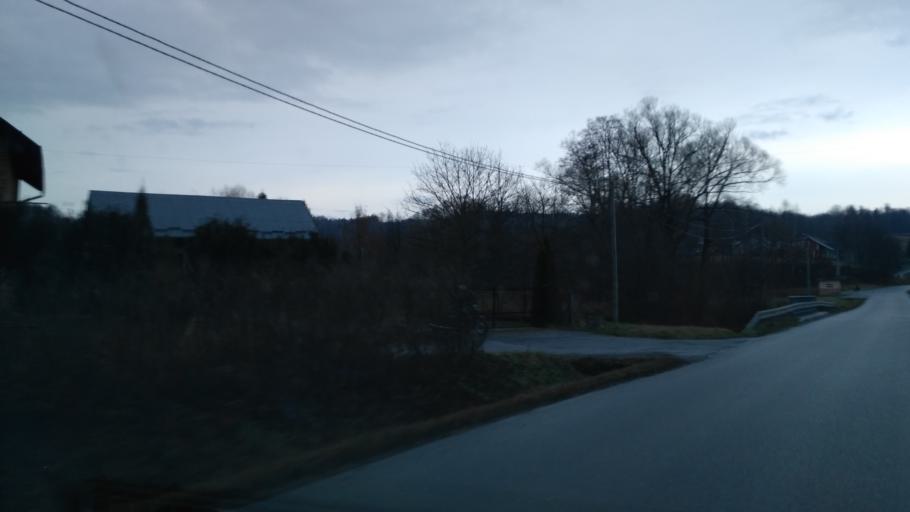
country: PL
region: Subcarpathian Voivodeship
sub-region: Powiat strzyzowski
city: Gwoznica Gorna
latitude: 49.8402
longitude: 21.9733
